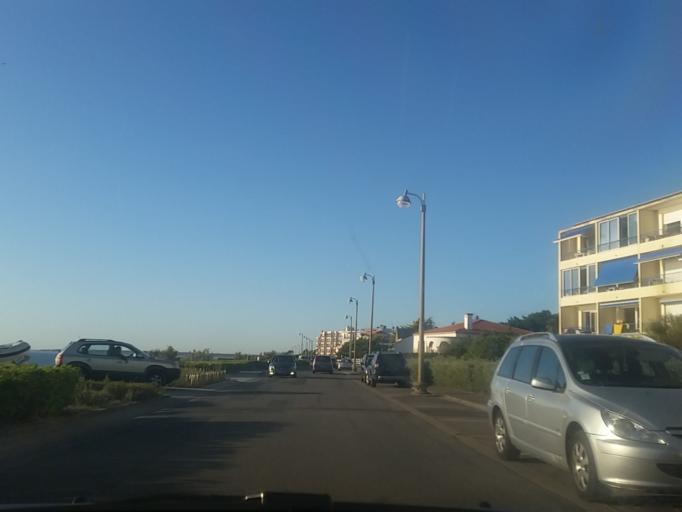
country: FR
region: Pays de la Loire
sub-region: Departement de la Loire-Atlantique
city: Saint-Michel-Chef-Chef
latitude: 47.1755
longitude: -2.1640
